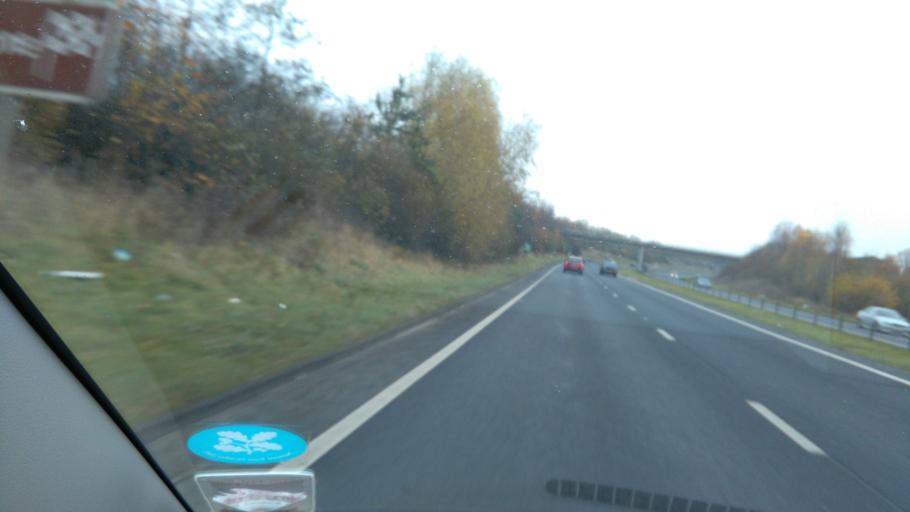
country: GB
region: England
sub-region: Northamptonshire
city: Silverstone
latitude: 52.0866
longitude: -1.0198
